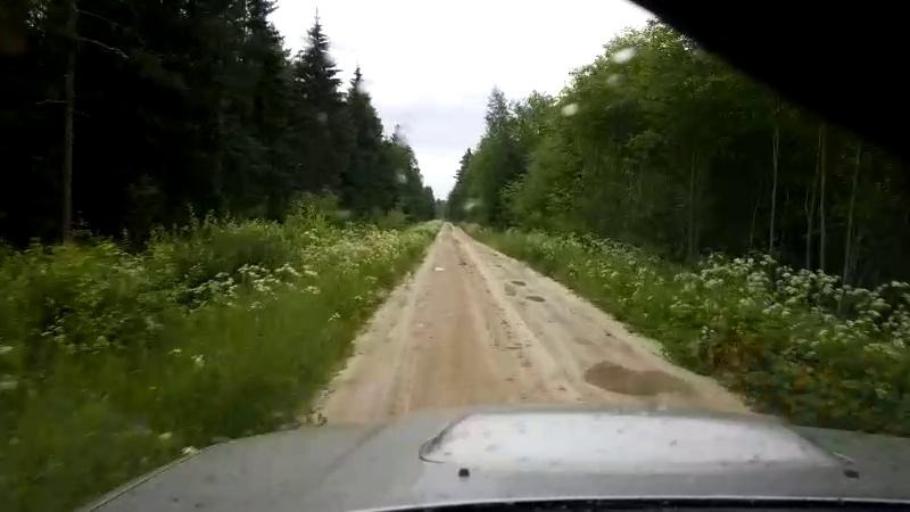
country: EE
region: Paernumaa
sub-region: Halinga vald
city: Parnu-Jaagupi
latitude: 58.5872
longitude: 24.6305
